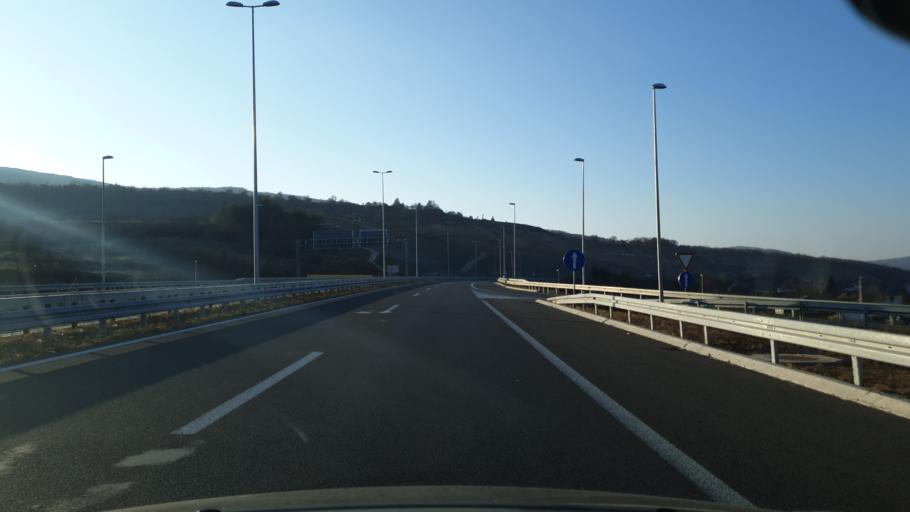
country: RS
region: Central Serbia
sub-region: Pirotski Okrug
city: Dimitrovgrad
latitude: 43.0020
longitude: 22.8123
